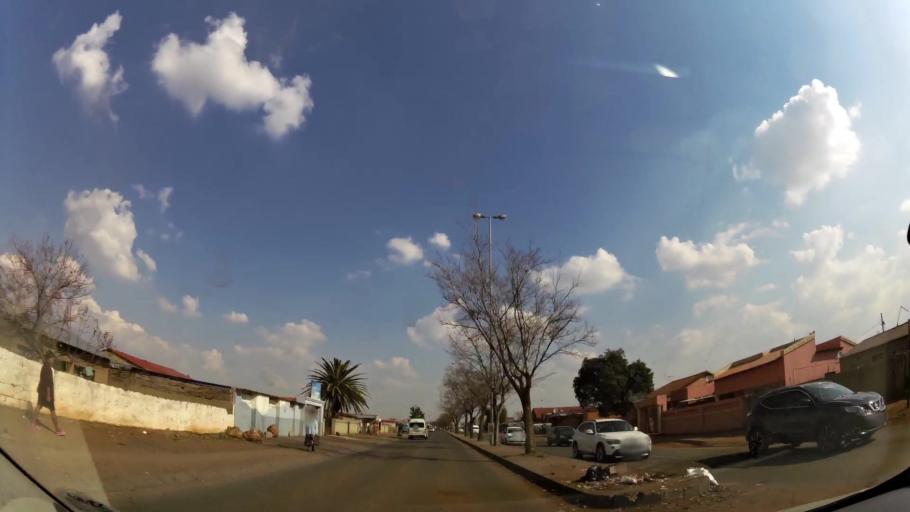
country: ZA
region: Gauteng
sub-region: Ekurhuleni Metropolitan Municipality
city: Germiston
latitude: -26.3241
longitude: 28.1551
